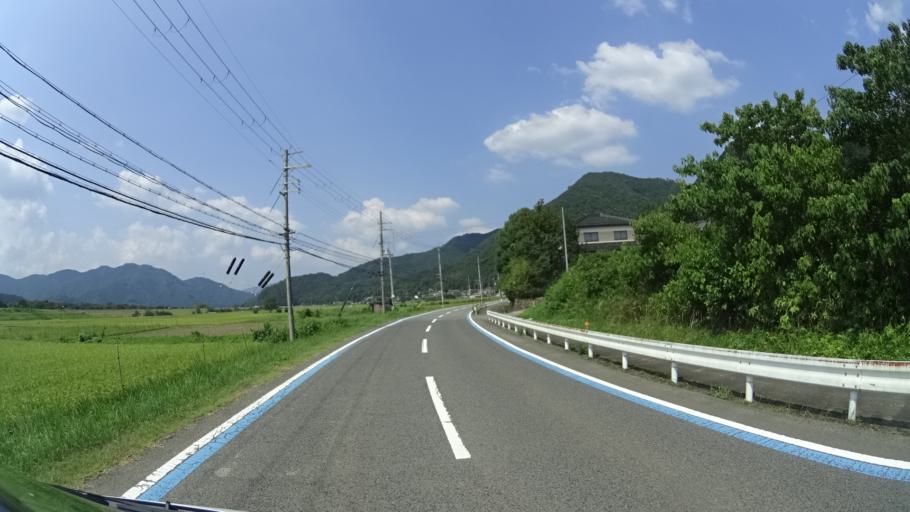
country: JP
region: Kyoto
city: Fukuchiyama
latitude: 35.3224
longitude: 135.1195
